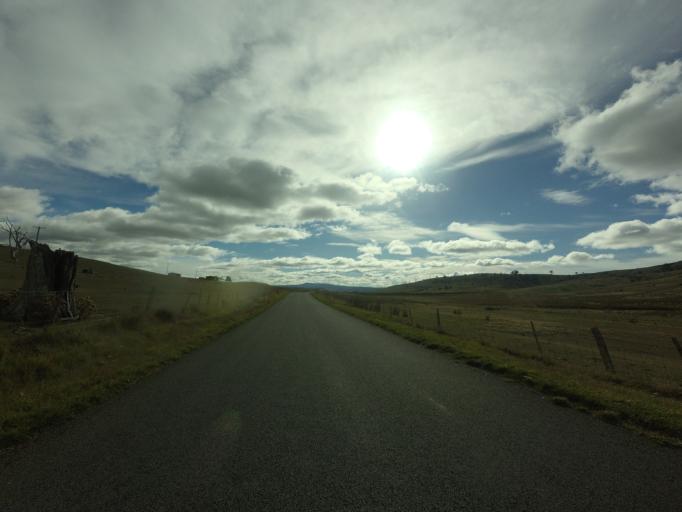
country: AU
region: Tasmania
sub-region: Brighton
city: Bridgewater
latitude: -42.3716
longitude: 147.3537
